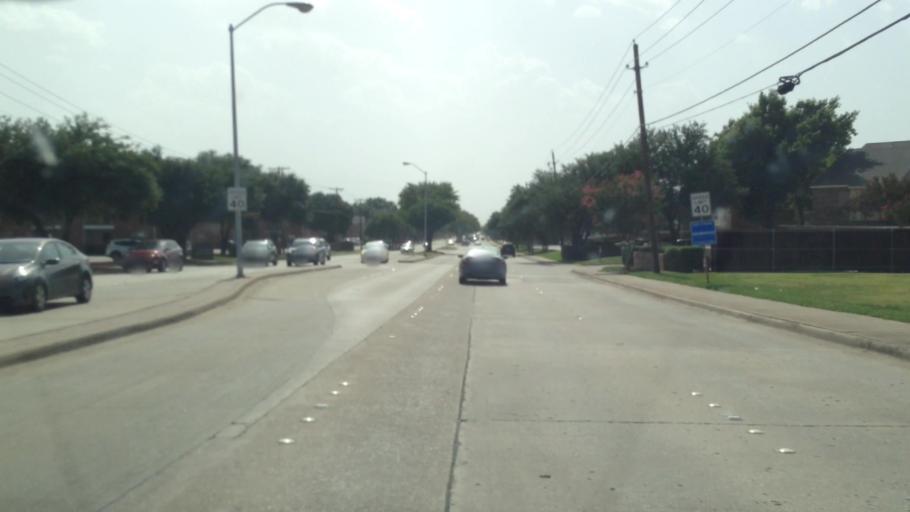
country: US
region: Texas
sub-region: Collin County
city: Plano
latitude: 33.0266
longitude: -96.7542
